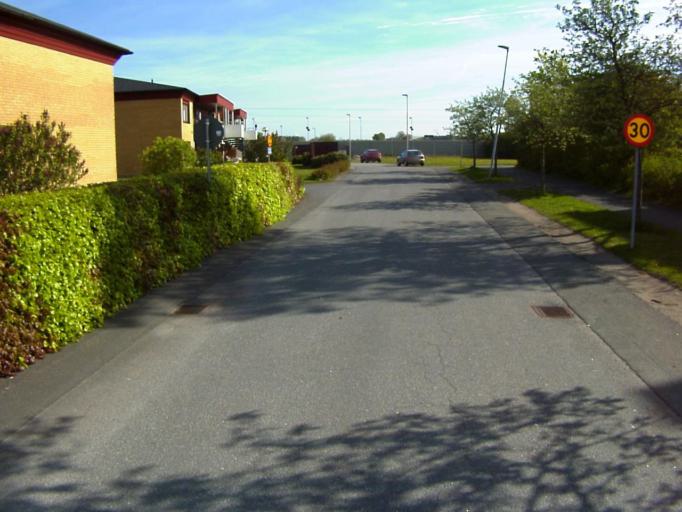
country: SE
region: Skane
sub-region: Kristianstads Kommun
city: Fjalkinge
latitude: 56.0426
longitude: 14.2809
